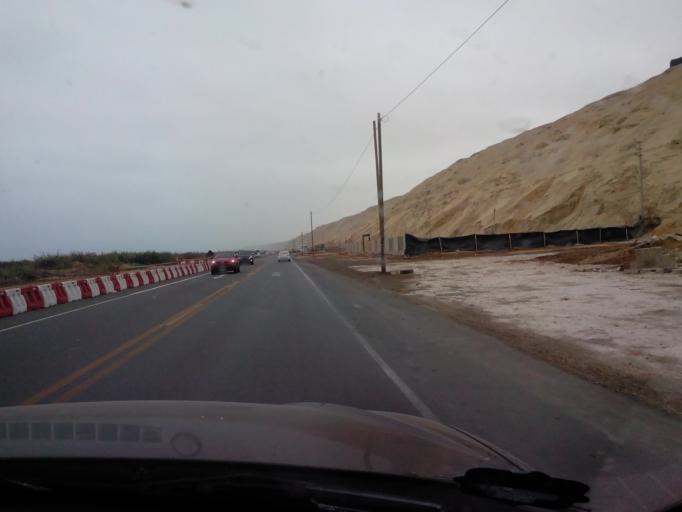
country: PE
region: Ica
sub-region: Provincia de Chincha
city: San Pedro
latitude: -13.4044
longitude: -76.1932
